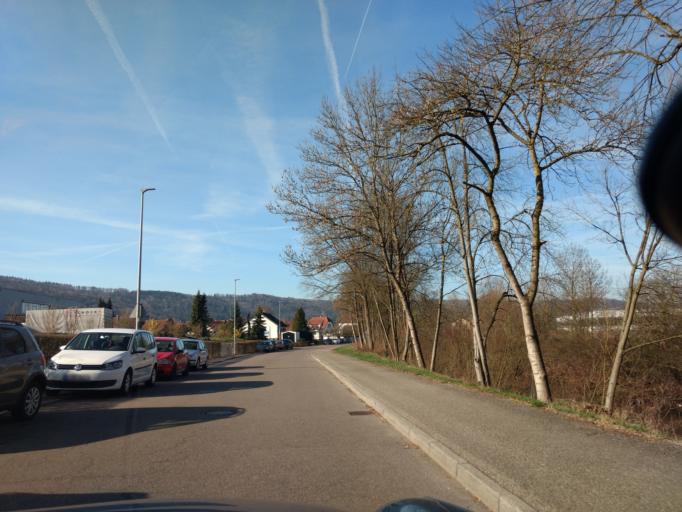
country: DE
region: Baden-Wuerttemberg
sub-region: Regierungsbezirk Stuttgart
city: Bortlingen
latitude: 48.7899
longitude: 9.6465
